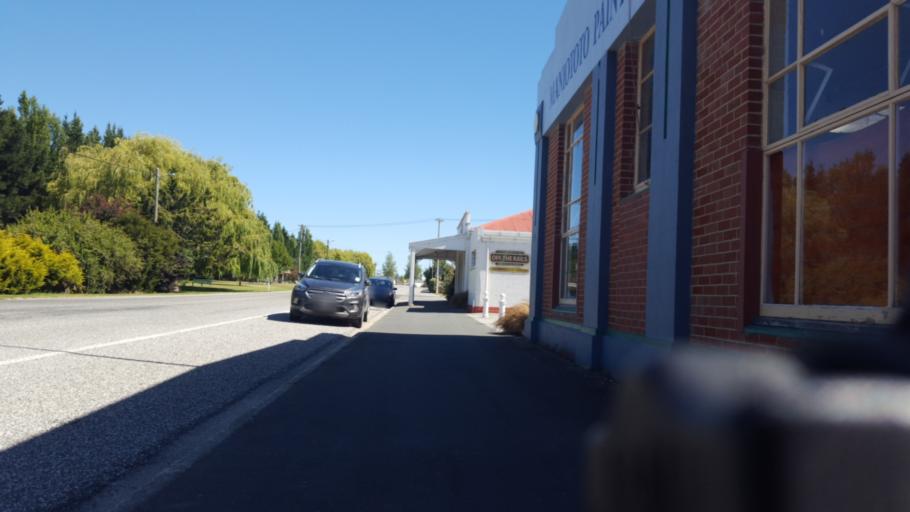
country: NZ
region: Otago
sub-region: Dunedin City
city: Dunedin
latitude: -45.1285
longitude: 170.0979
